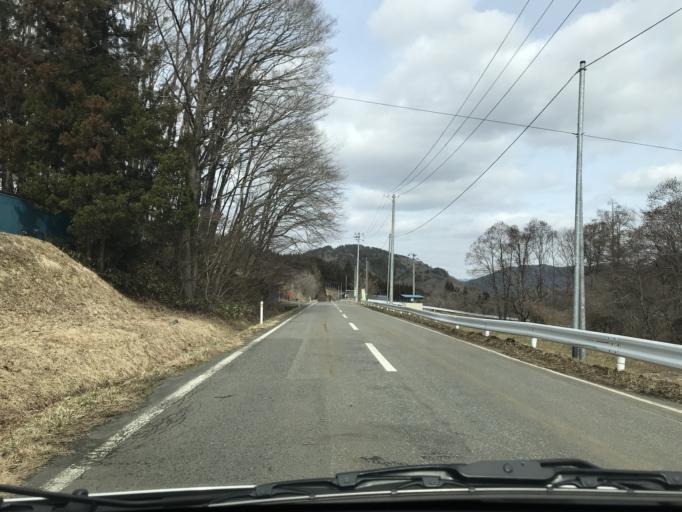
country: JP
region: Iwate
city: Kitakami
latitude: 39.2721
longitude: 141.3204
